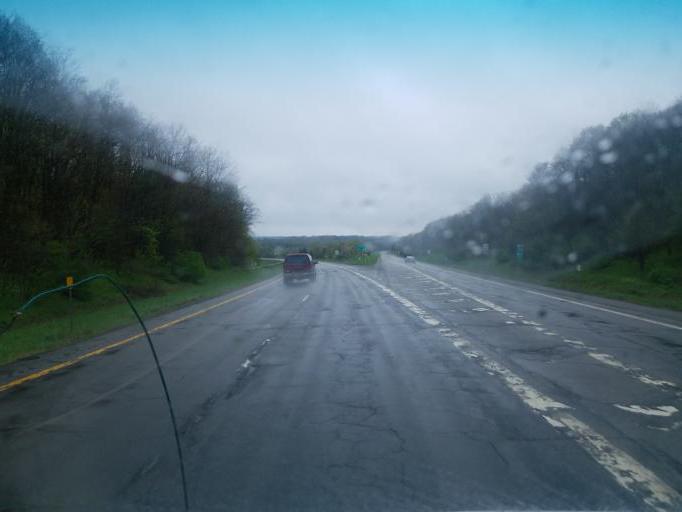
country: US
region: New York
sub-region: Chautauqua County
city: Lakewood
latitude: 42.1518
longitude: -79.3682
